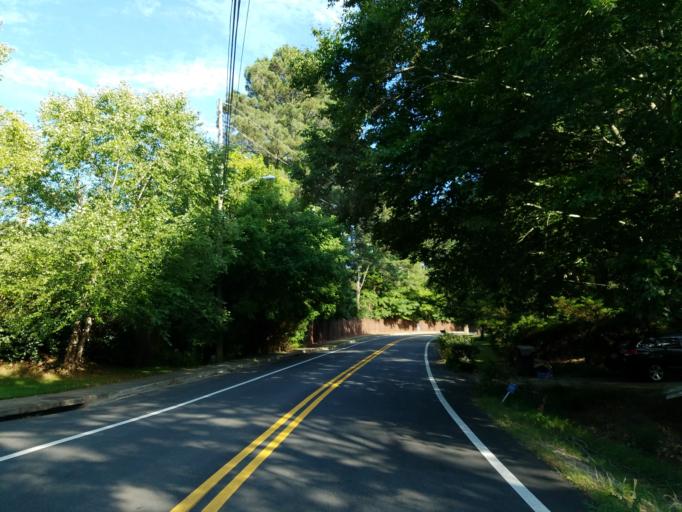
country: US
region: Georgia
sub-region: Fulton County
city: Roswell
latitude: 33.9955
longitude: -84.4439
